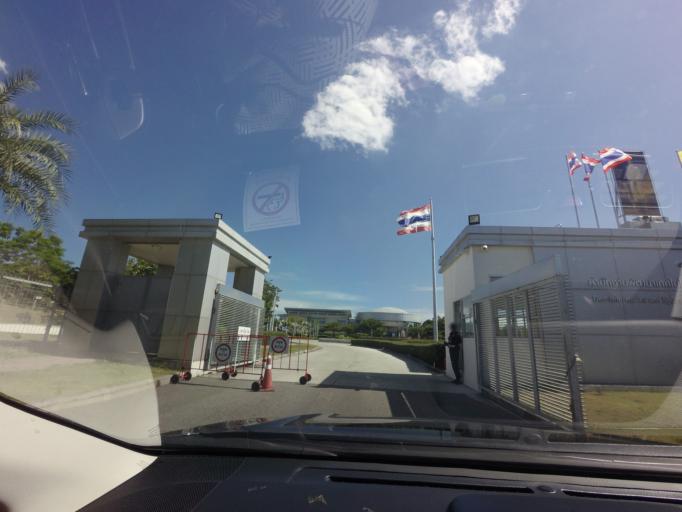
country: TH
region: Chon Buri
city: Bang Lamung
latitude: 13.1036
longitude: 100.9284
